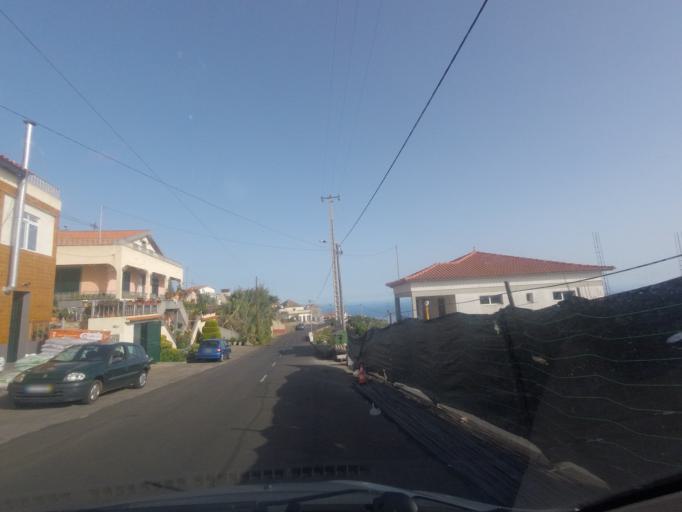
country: PT
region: Madeira
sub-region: Calheta
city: Arco da Calheta
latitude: 32.7019
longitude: -17.1253
